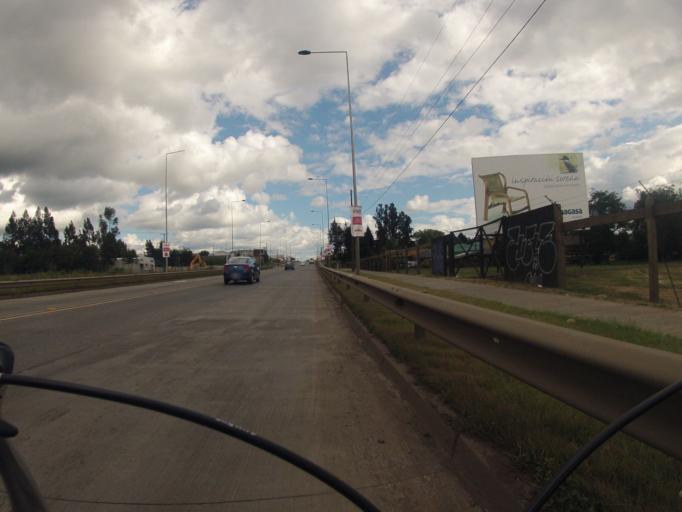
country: CL
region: Araucania
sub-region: Provincia de Cautin
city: Temuco
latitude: -38.7601
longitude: -72.6094
